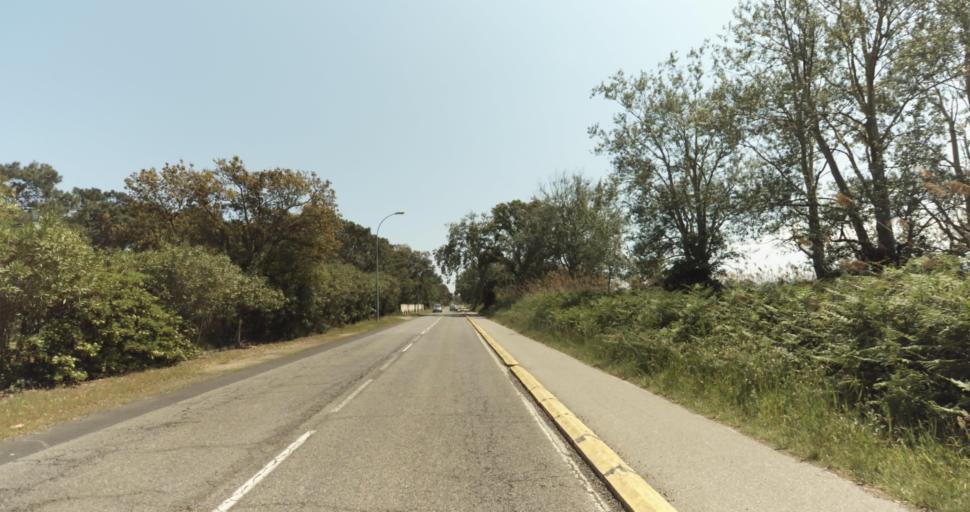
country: FR
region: Corsica
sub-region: Departement de la Haute-Corse
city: Biguglia
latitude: 42.6327
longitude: 9.4640
